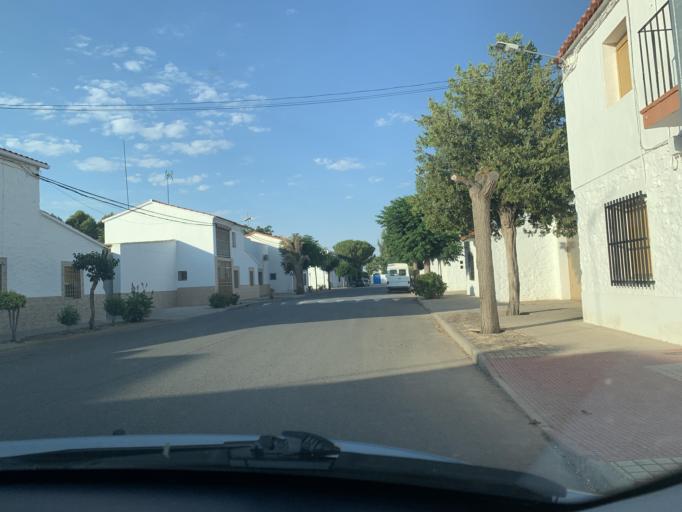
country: ES
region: Castille-La Mancha
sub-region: Provincia de Ciudad Real
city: Argamasilla de Alba
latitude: 39.1752
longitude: -3.2355
